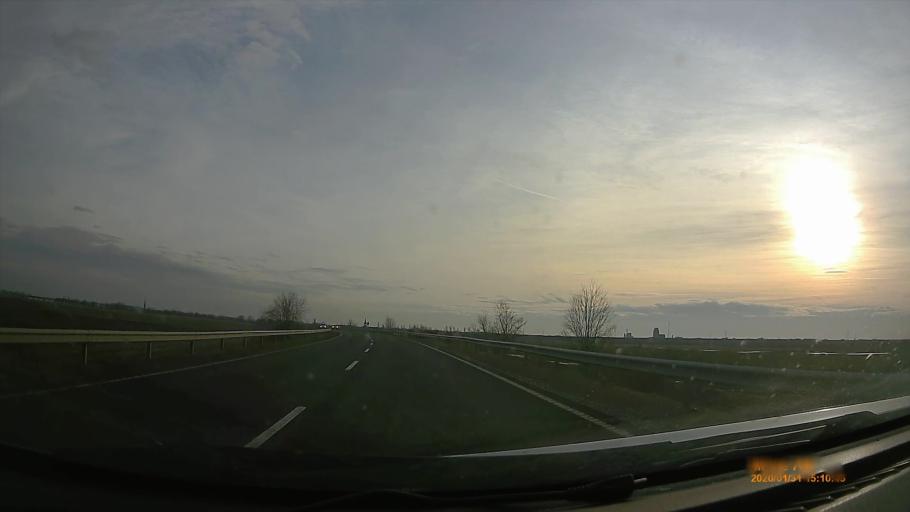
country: HU
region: Hajdu-Bihar
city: Polgar
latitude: 47.8577
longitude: 21.1504
